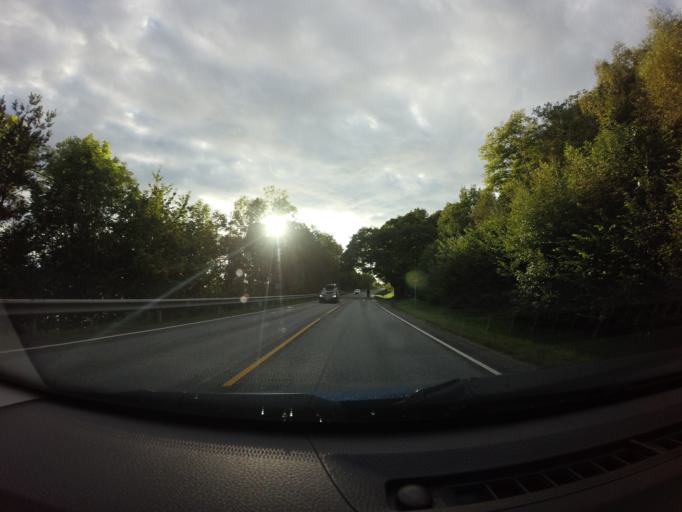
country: NO
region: Rogaland
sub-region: Strand
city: Tau
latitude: 59.0247
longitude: 5.9740
